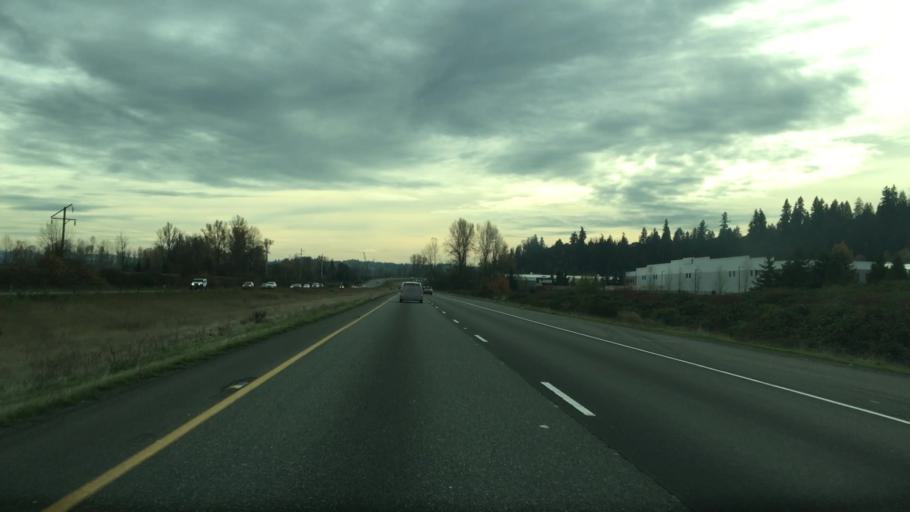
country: US
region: Washington
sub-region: Pierce County
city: Sumner
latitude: 47.2172
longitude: -122.2473
